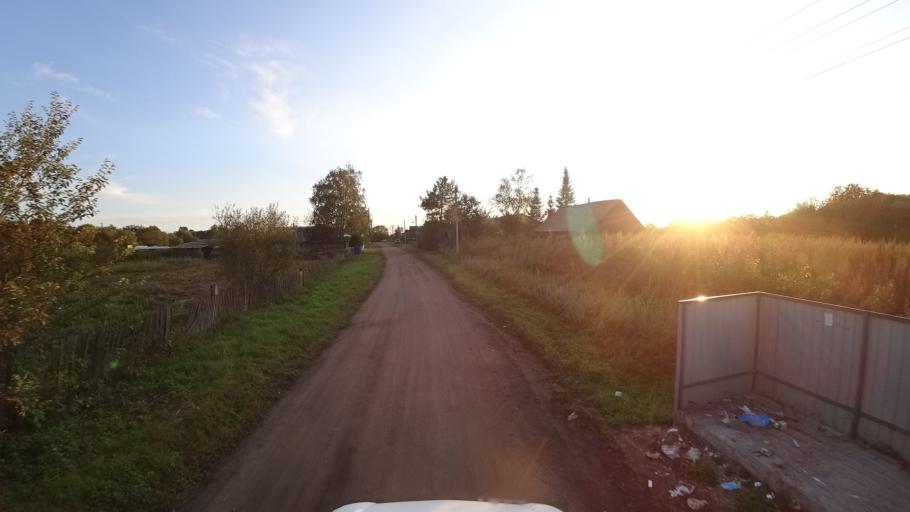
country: RU
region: Amur
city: Arkhara
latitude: 49.3655
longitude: 130.1150
